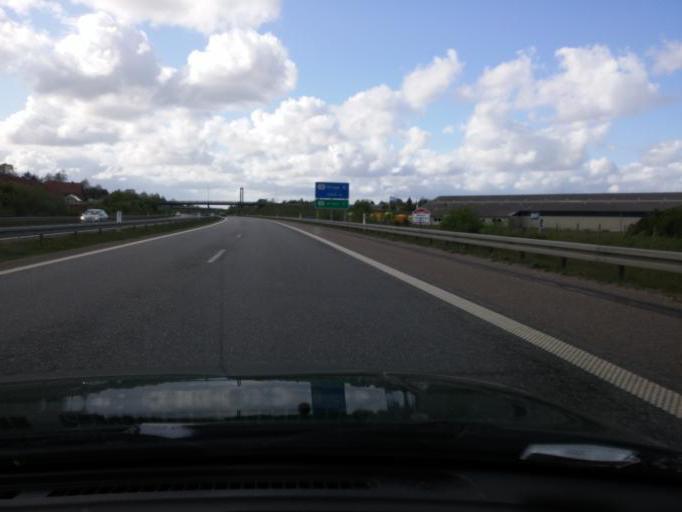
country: DK
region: South Denmark
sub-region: Faaborg-Midtfyn Kommune
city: Ringe
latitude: 55.2425
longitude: 10.4871
